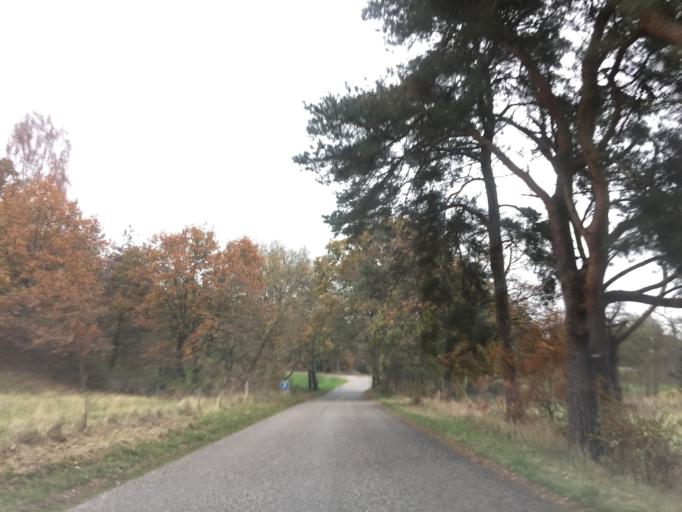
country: DK
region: Central Jutland
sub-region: Silkeborg Kommune
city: Svejbaek
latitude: 56.2027
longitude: 9.6473
